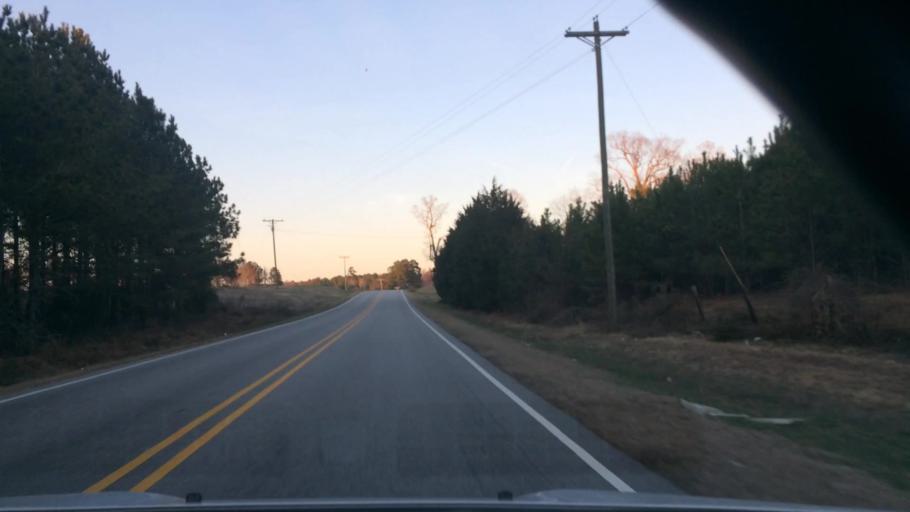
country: US
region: North Carolina
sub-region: Wake County
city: Rolesville
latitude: 35.9807
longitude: -78.4204
